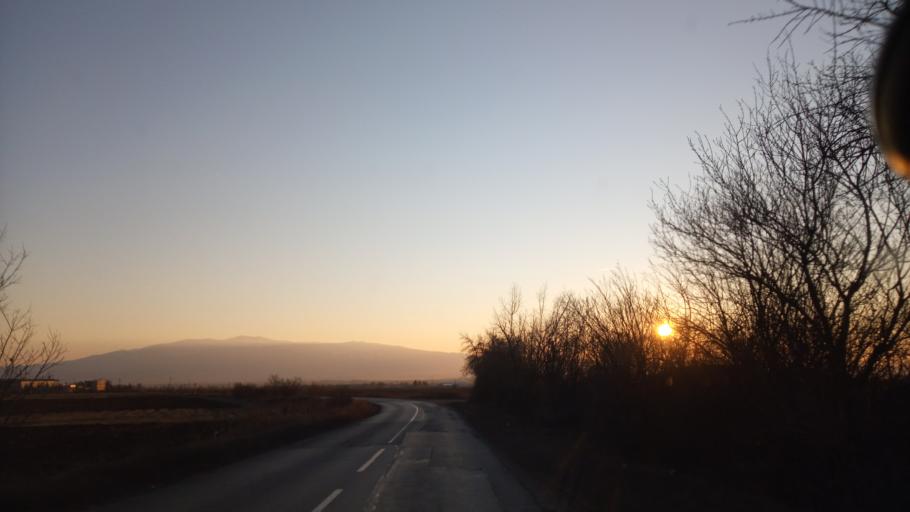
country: BG
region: Sofia-Capital
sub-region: Stolichna Obshtina
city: Bukhovo
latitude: 42.7682
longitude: 23.4937
